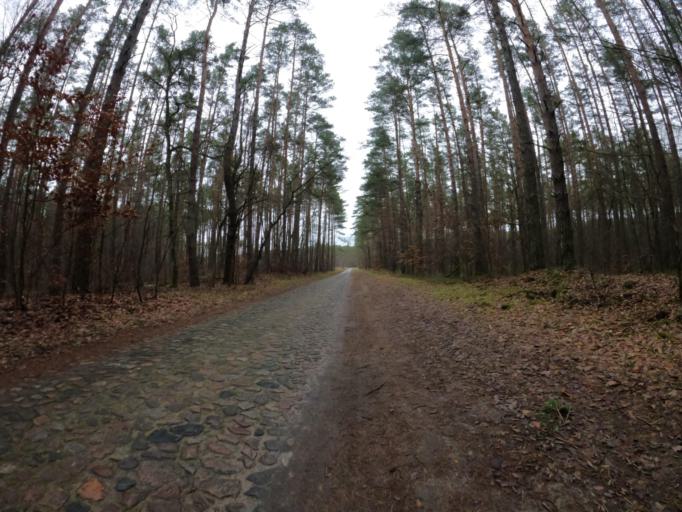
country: PL
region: West Pomeranian Voivodeship
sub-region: Powiat mysliborski
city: Debno
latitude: 52.7112
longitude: 14.7224
